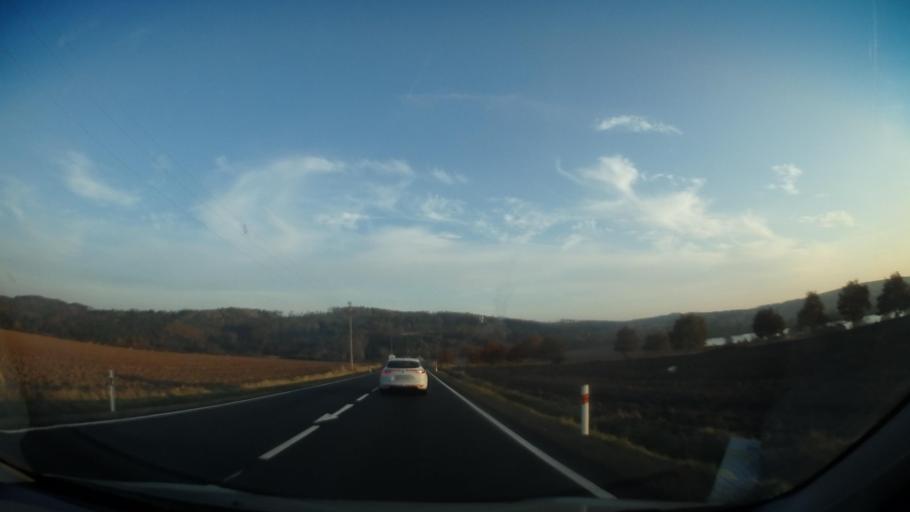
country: CZ
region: Central Bohemia
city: Postupice
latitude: 49.7330
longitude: 14.8258
